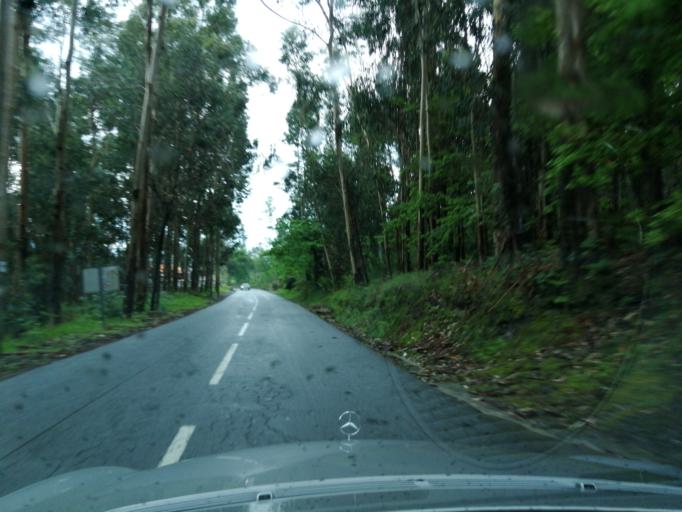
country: PT
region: Braga
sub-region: Vila Nova de Famalicao
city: Joane
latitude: 41.4722
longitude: -8.4283
